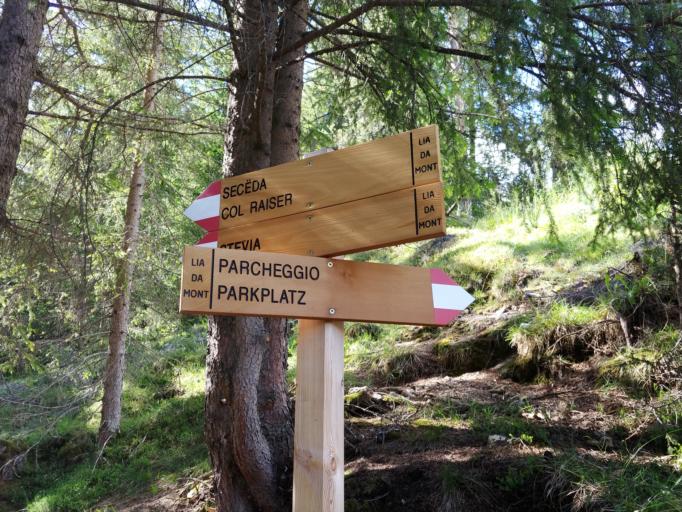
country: IT
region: Trentino-Alto Adige
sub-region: Bolzano
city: Selva
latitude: 46.5637
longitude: 11.7527
